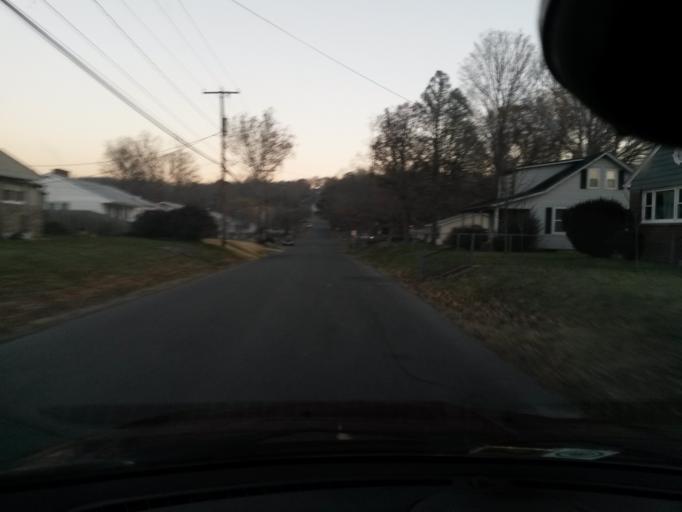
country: US
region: Virginia
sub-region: Alleghany County
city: Clifton Forge
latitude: 37.8265
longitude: -79.8210
